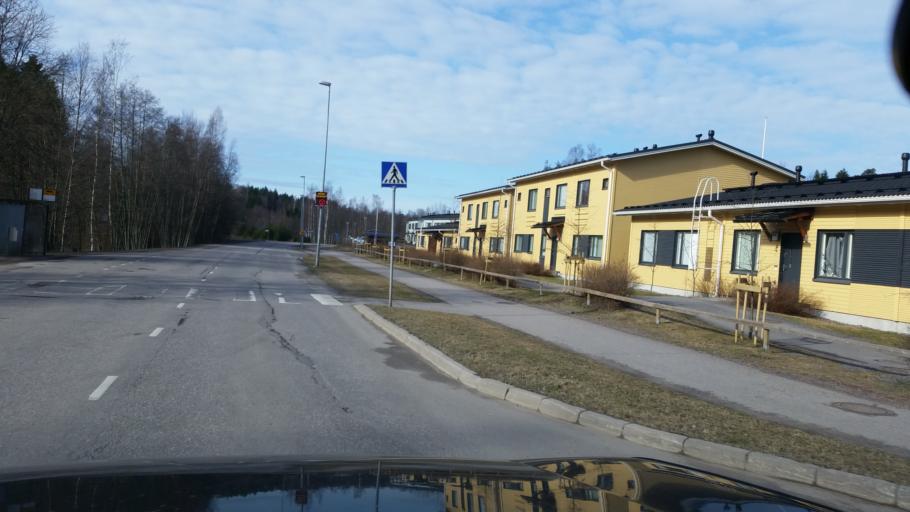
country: FI
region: Uusimaa
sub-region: Helsinki
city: Kirkkonummi
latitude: 60.0938
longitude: 24.4025
